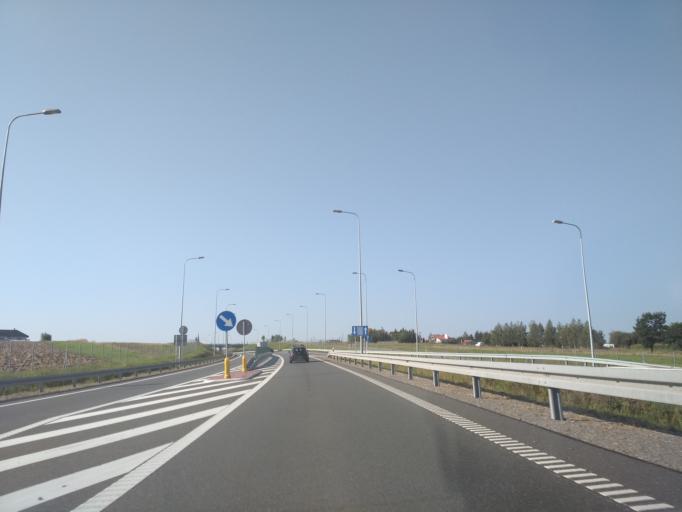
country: PL
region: Subcarpathian Voivodeship
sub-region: Powiat rzeszowski
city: Sokolow Malopolski
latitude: 50.2023
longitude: 22.1064
